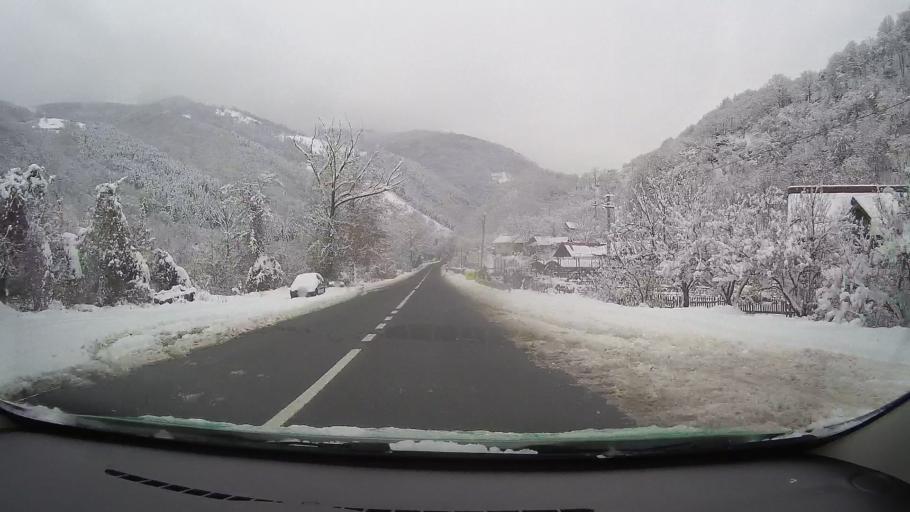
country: RO
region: Alba
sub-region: Comuna Sasciori
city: Sasciori
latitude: 45.8272
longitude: 23.6063
